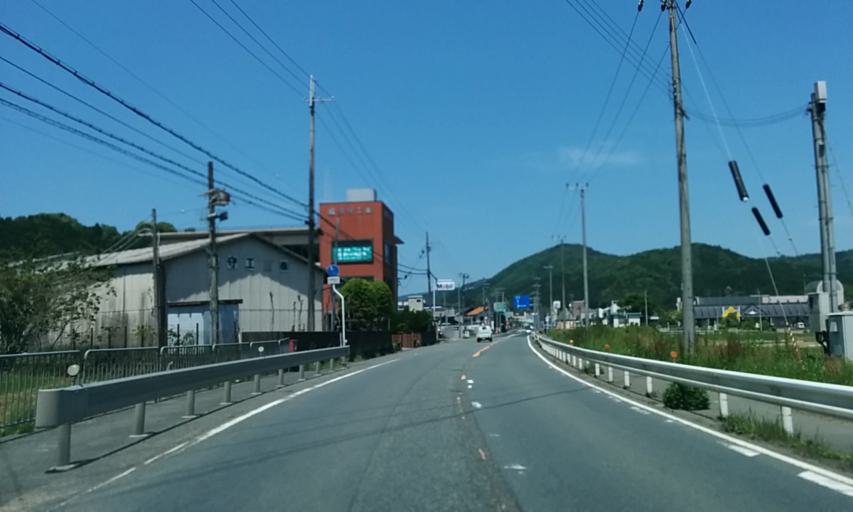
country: JP
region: Kyoto
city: Fukuchiyama
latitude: 35.3873
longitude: 135.1451
